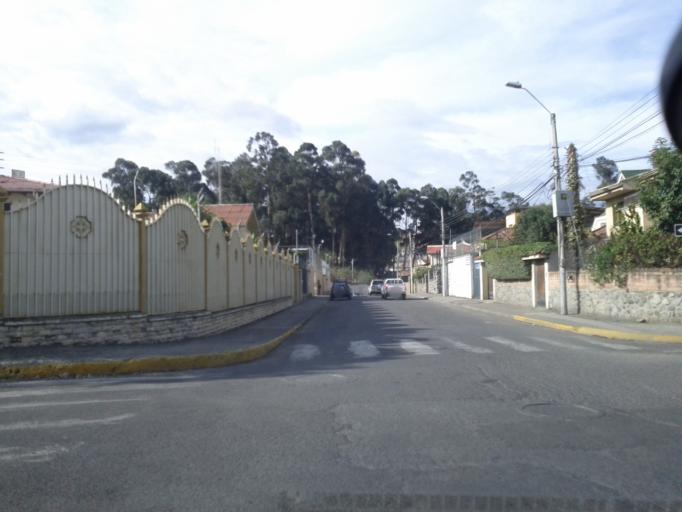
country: EC
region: Azuay
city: Cuenca
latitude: -2.8969
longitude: -79.0172
